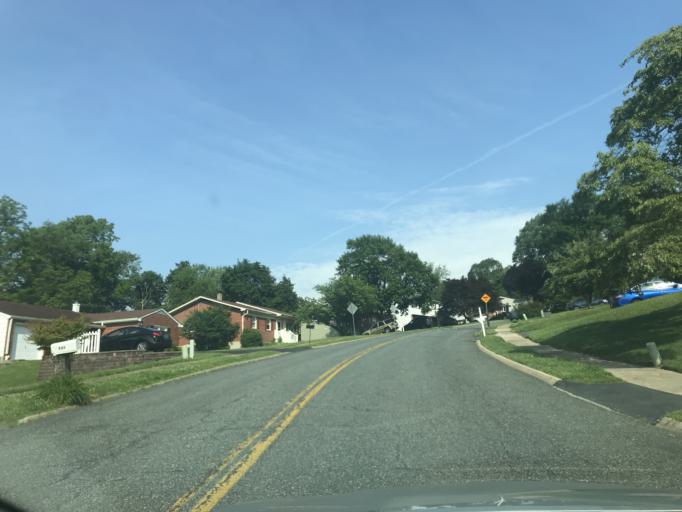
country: US
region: Maryland
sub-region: Harford County
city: Bel Air North
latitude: 39.5553
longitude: -76.3872
